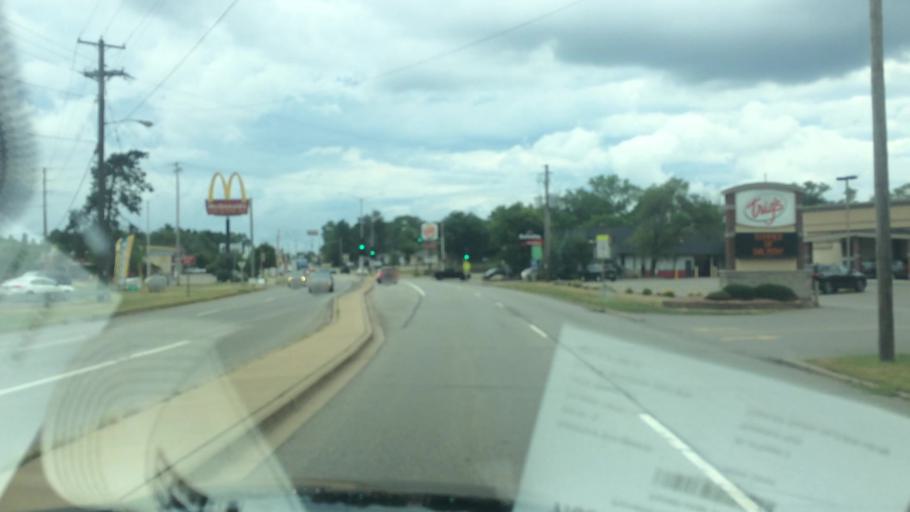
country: US
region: Wisconsin
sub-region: Marathon County
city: Schofield
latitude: 44.9008
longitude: -89.6087
